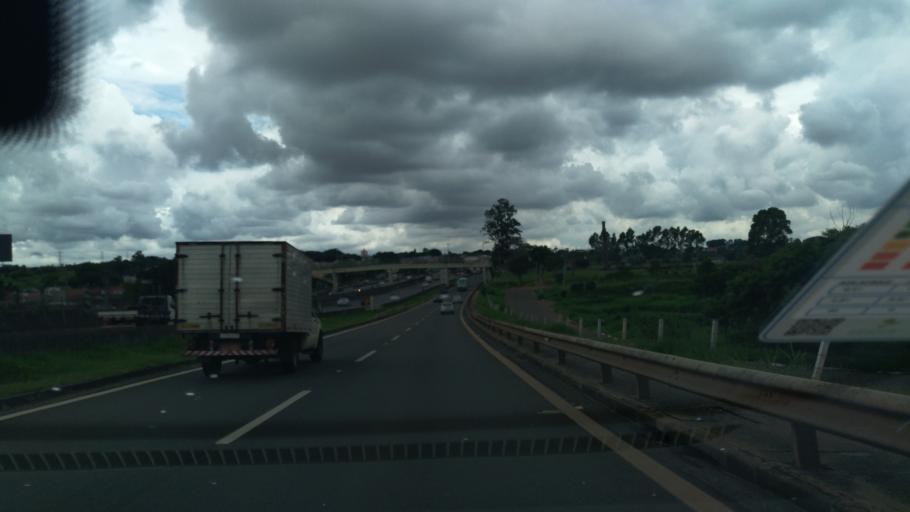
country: BR
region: Sao Paulo
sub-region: Campinas
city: Campinas
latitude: -22.8791
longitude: -47.1193
